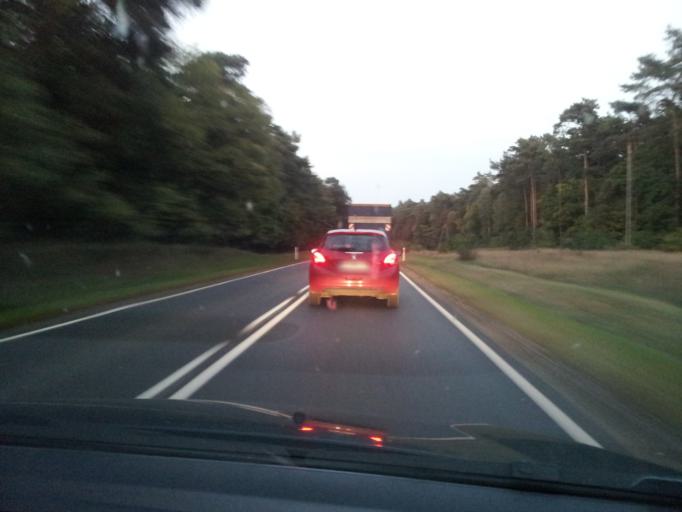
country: PL
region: Kujawsko-Pomorskie
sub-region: Powiat torunski
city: Wielka Nieszawka
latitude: 52.9168
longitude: 18.4933
